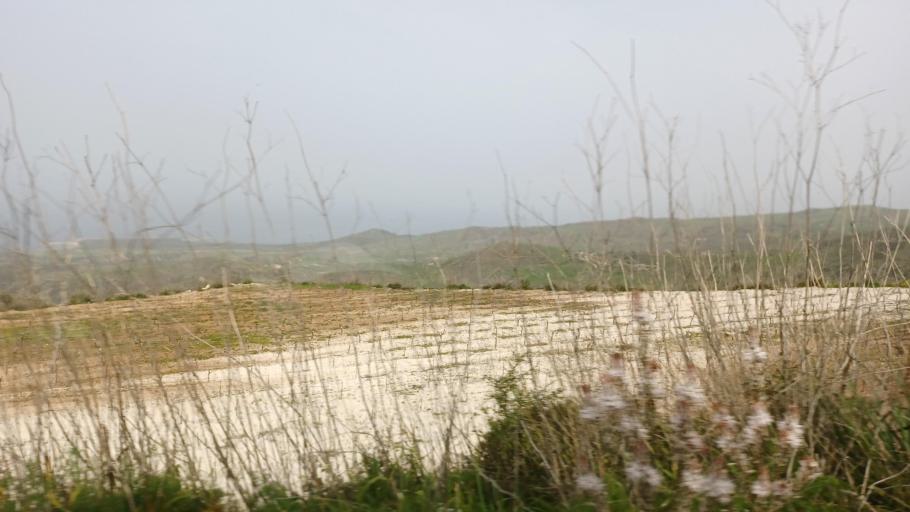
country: CY
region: Pafos
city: Pegeia
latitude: 34.9453
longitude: 32.3749
